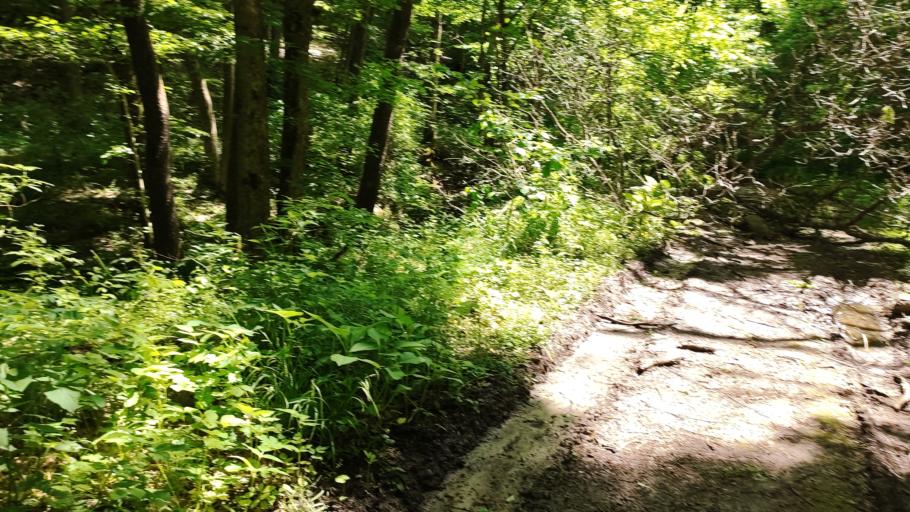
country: RU
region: Krasnodarskiy
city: Goryachiy Klyuch
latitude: 44.6810
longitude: 38.9778
